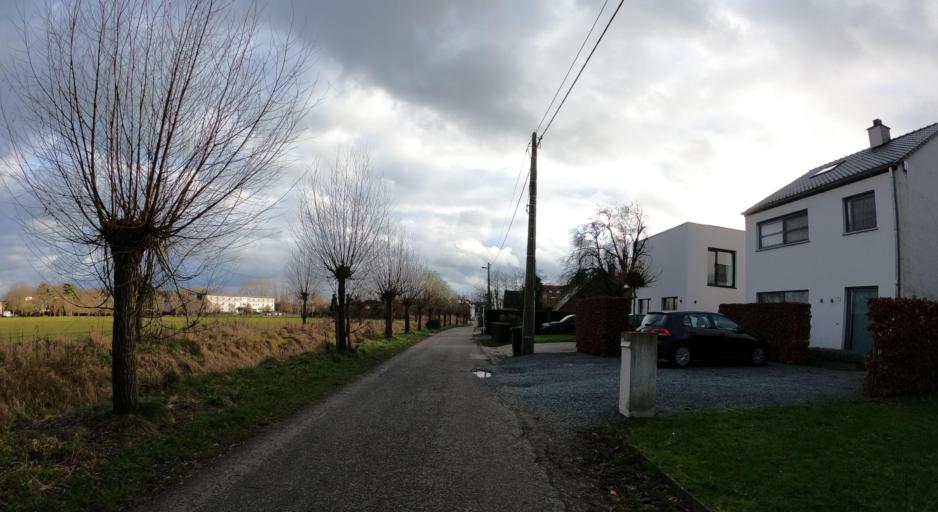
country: BE
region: Flanders
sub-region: Provincie Antwerpen
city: Edegem
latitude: 51.1517
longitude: 4.4297
